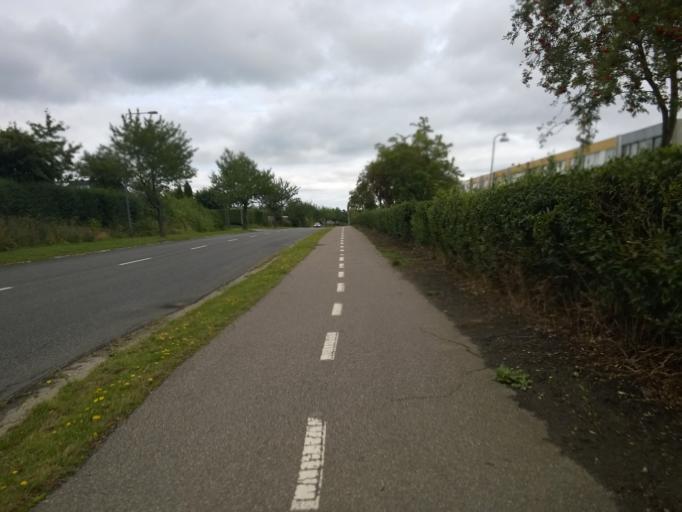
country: DK
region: Capital Region
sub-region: Egedal Kommune
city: Smorumnedre
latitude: 55.7478
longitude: 12.3062
